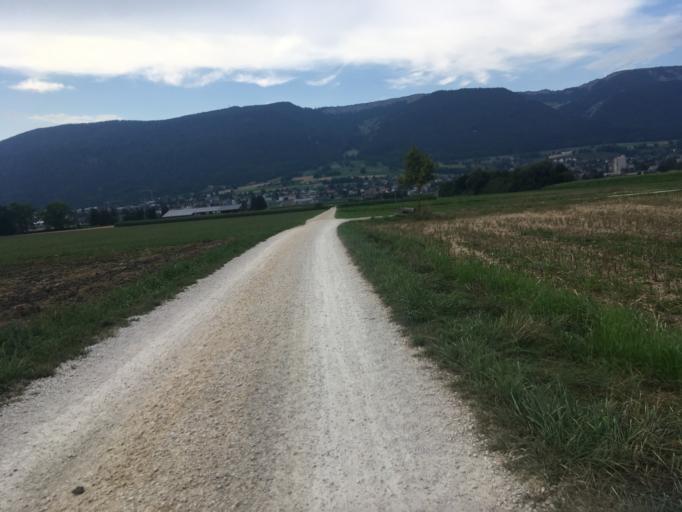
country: CH
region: Solothurn
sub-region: Bezirk Lebern
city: Bettlach
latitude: 47.1846
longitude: 7.4260
